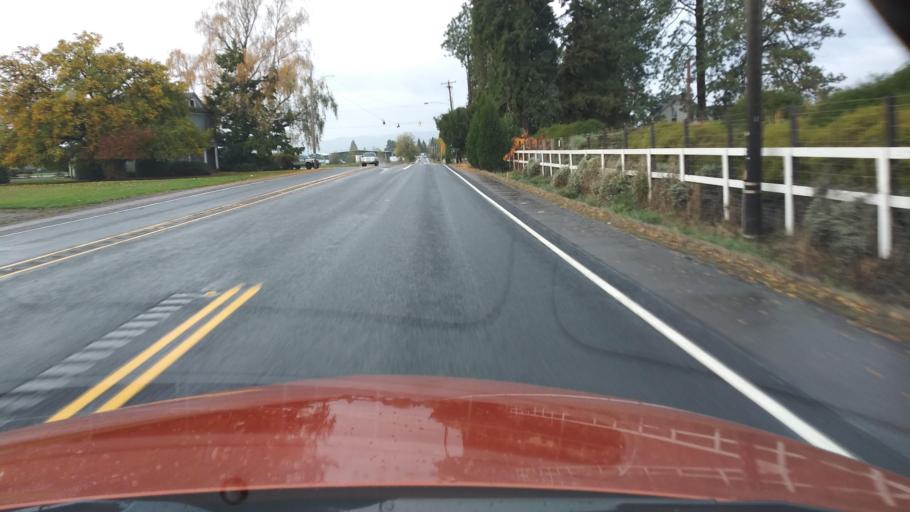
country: US
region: Oregon
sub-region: Washington County
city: North Plains
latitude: 45.5733
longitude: -123.0345
